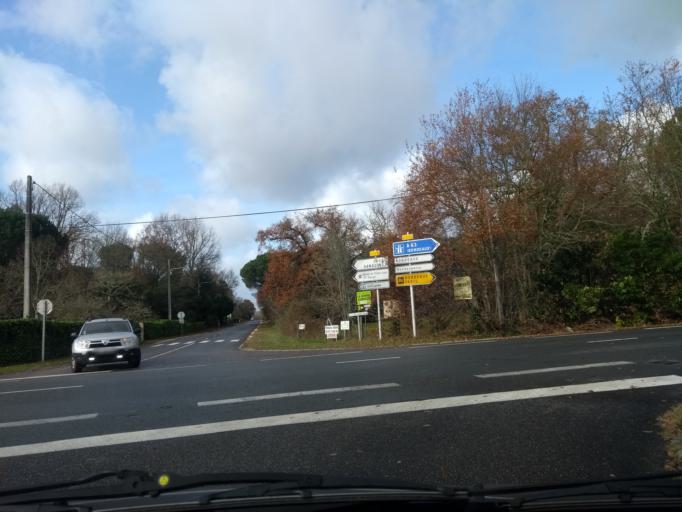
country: FR
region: Aquitaine
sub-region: Departement de la Gironde
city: Belin-Beliet
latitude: 44.4891
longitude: -0.7915
